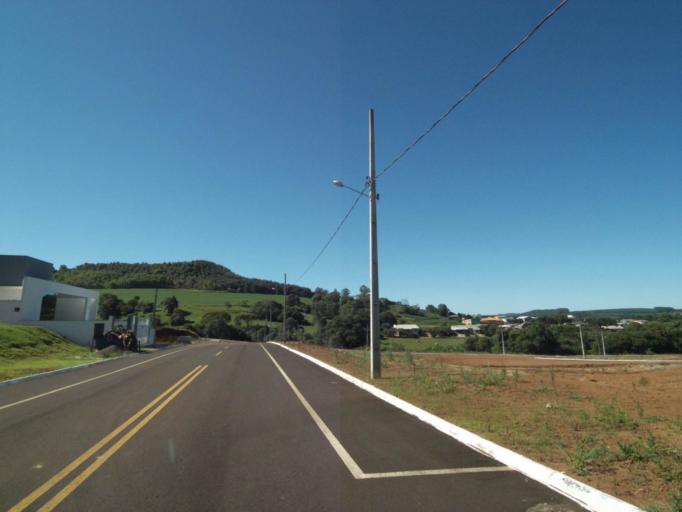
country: BR
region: Parana
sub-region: Pato Branco
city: Pato Branco
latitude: -26.2629
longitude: -52.7728
